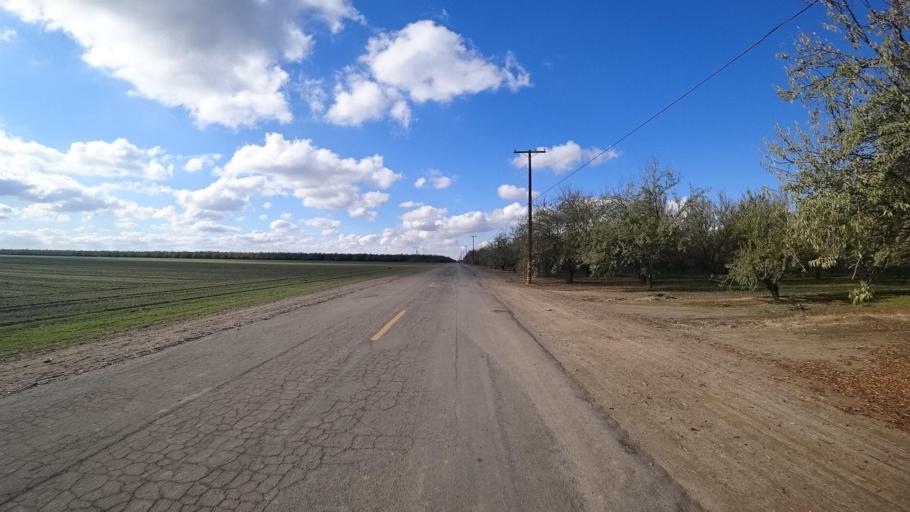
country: US
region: California
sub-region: Kern County
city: McFarland
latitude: 35.6812
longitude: -119.2646
